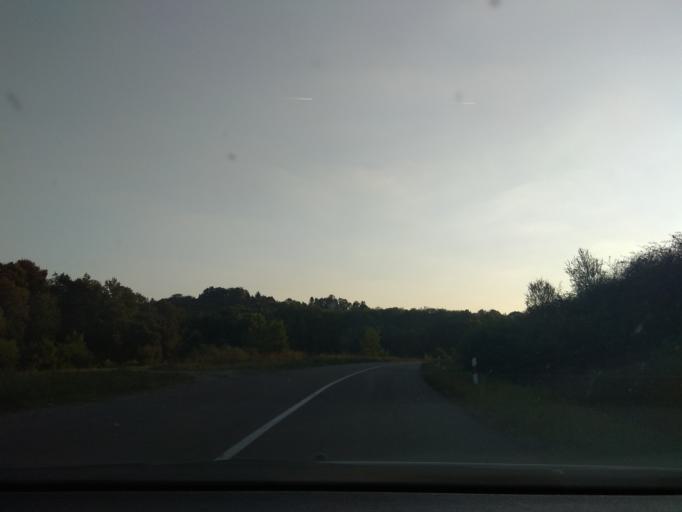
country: HU
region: Heves
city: Eger
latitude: 47.8648
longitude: 20.3725
